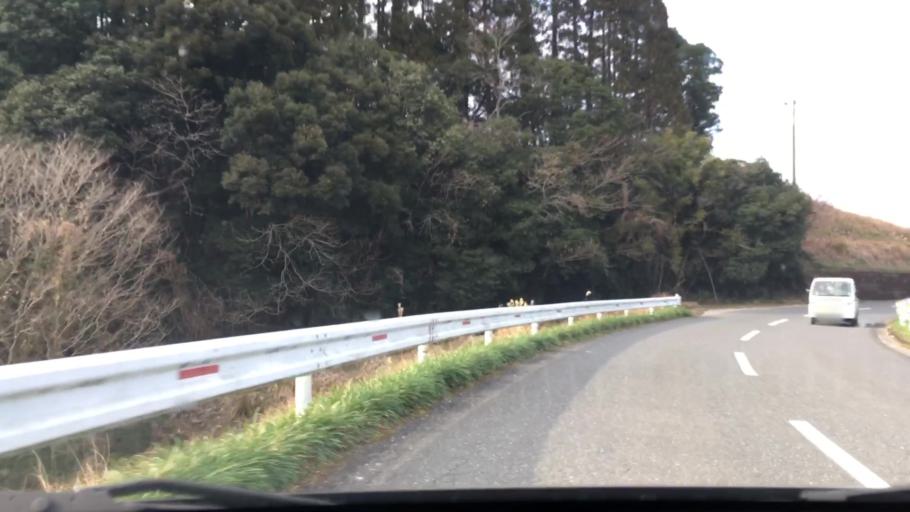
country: JP
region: Miyazaki
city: Nichinan
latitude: 31.6171
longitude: 131.3355
